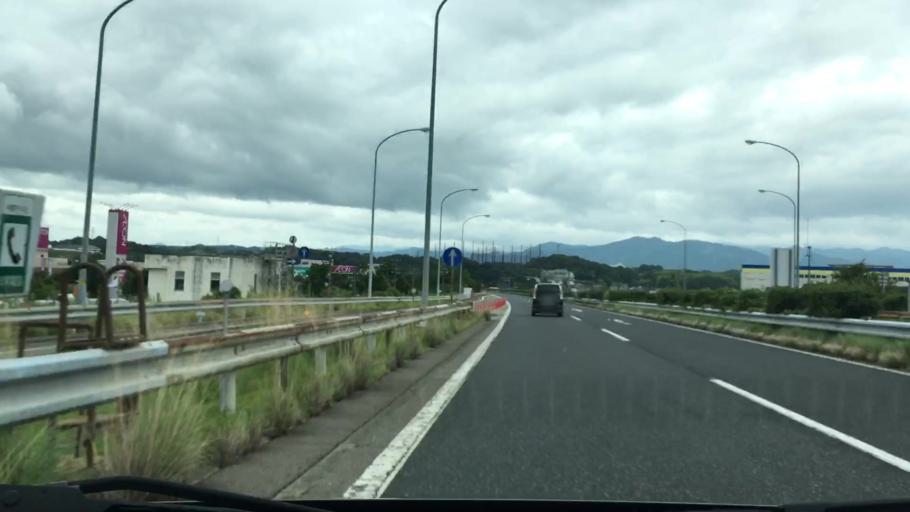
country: JP
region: Okayama
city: Tsuyama
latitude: 35.0635
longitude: 134.0505
